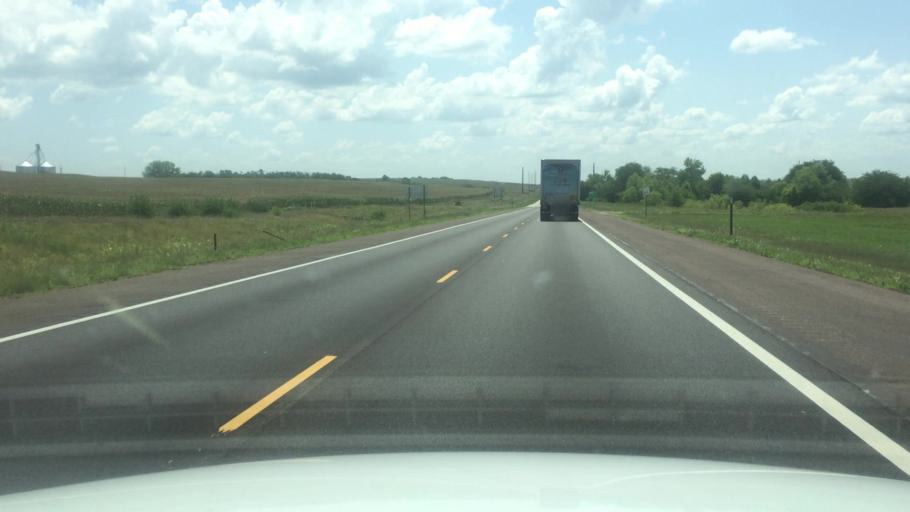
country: US
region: Kansas
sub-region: Nemaha County
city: Sabetha
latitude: 39.8334
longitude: -95.7334
